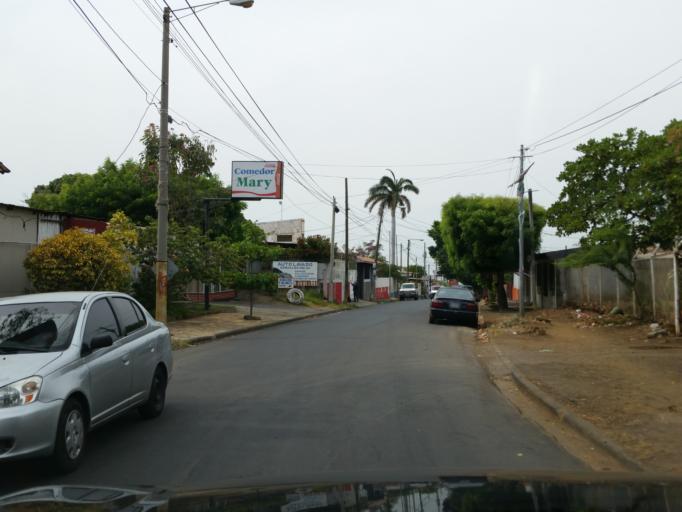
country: NI
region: Managua
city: Managua
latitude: 12.1164
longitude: -86.2551
